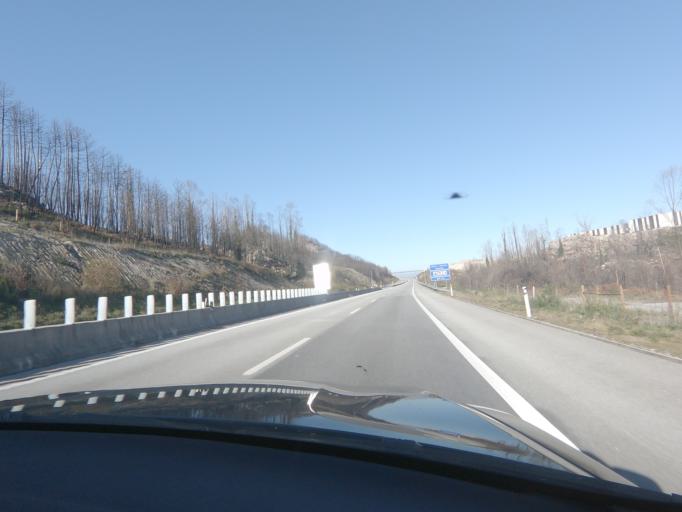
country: PT
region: Viseu
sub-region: Vouzela
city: Vouzela
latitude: 40.6566
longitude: -8.0761
